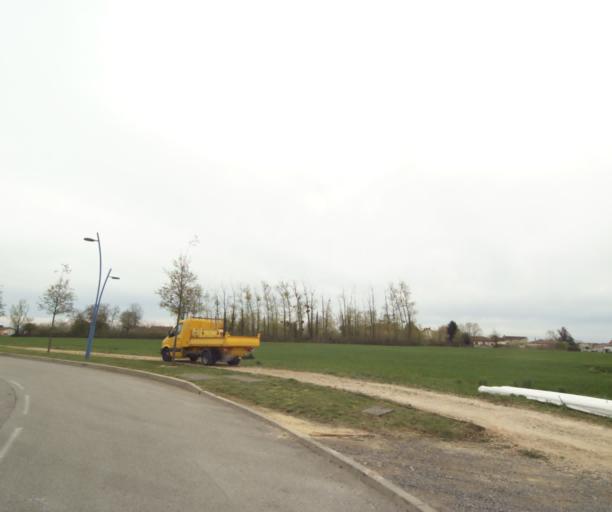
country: FR
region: Bourgogne
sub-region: Departement de Saone-et-Loire
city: Charnay-les-Macon
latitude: 46.2989
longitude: 4.8025
